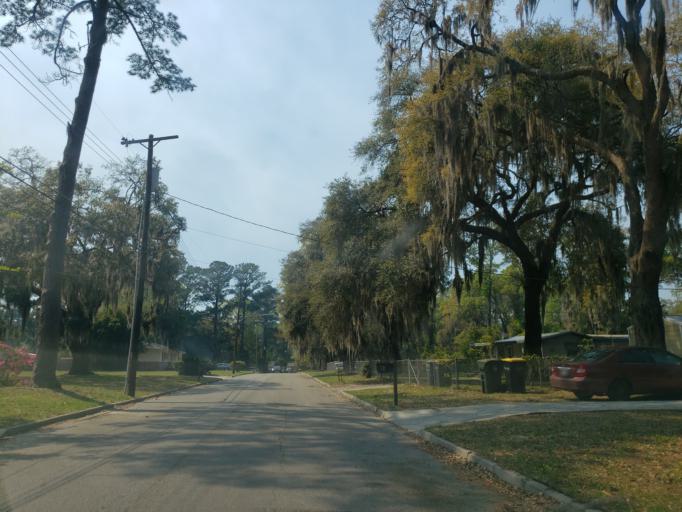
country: US
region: Georgia
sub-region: Chatham County
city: Isle of Hope
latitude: 32.0088
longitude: -81.0711
